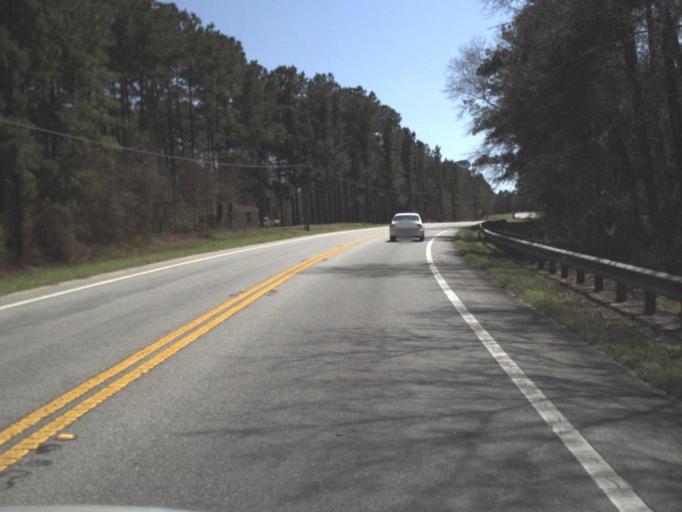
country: US
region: Florida
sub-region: Gadsden County
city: Quincy
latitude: 30.6231
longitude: -84.5951
